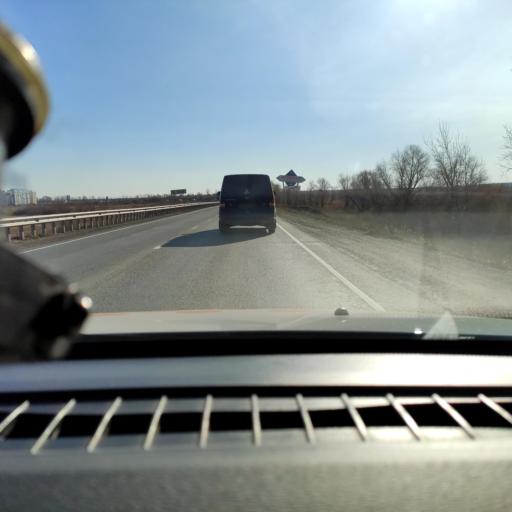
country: RU
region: Samara
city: Samara
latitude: 53.0981
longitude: 50.1439
